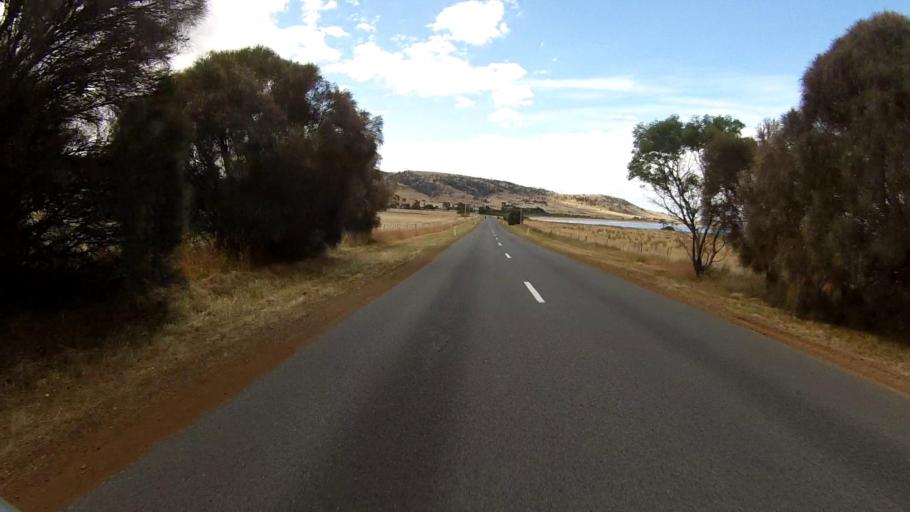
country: AU
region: Tasmania
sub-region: Sorell
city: Sorell
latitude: -42.2090
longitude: 148.0401
